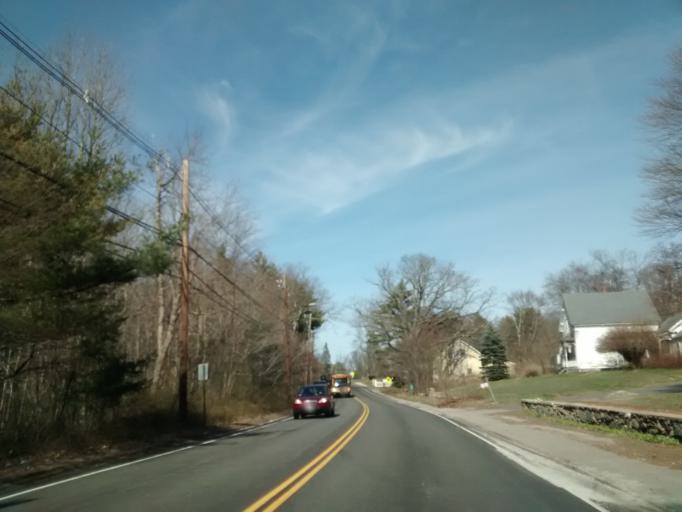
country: US
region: Massachusetts
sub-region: Norfolk County
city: Bellingham
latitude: 42.1272
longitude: -71.4530
